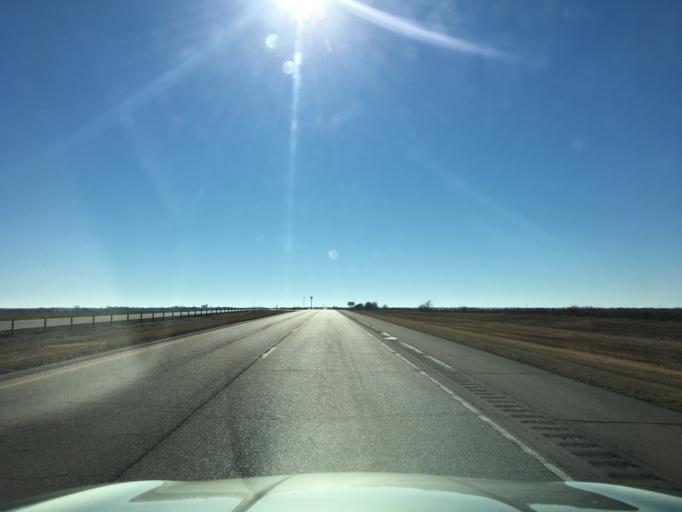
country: US
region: Oklahoma
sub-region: Kay County
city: Blackwell
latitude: 36.9687
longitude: -97.3458
